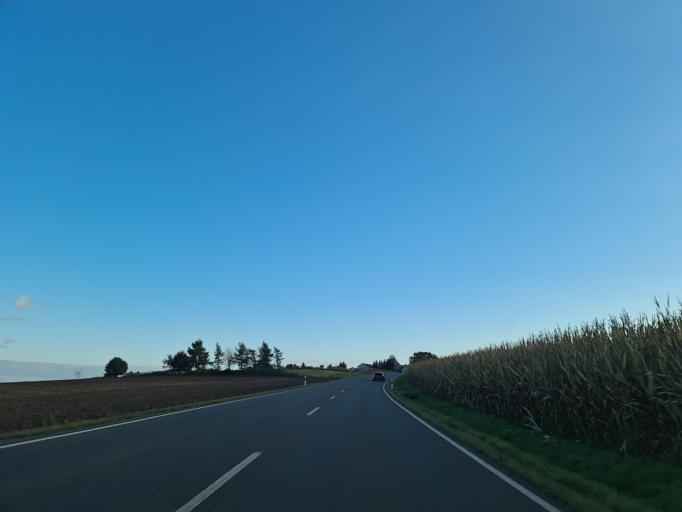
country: DE
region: Thuringia
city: Wildetaube
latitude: 50.7111
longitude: 12.1167
